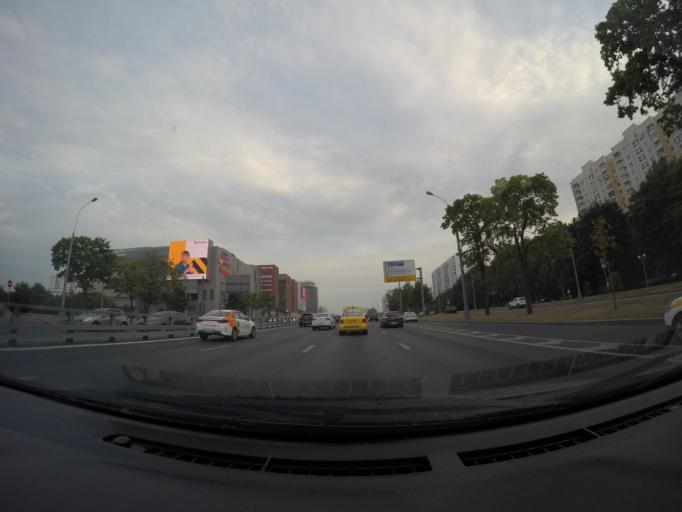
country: RU
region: Moscow
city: Orekhovo-Borisovo
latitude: 55.6232
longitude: 37.7112
